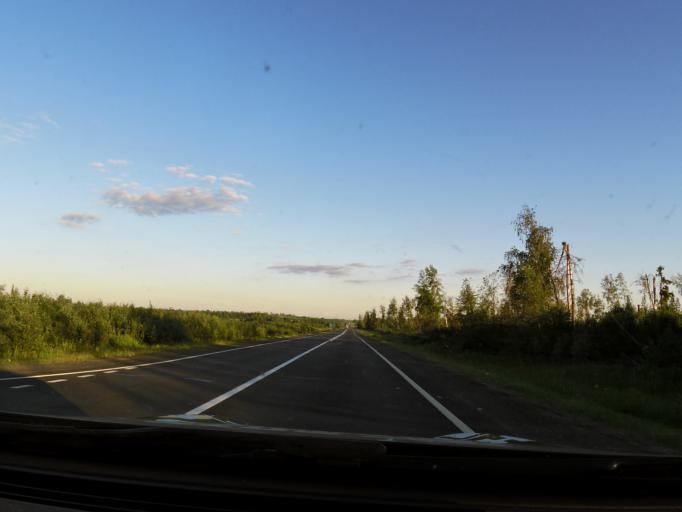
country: RU
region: Jaroslavl
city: Prechistoye
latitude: 58.6052
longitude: 40.3394
